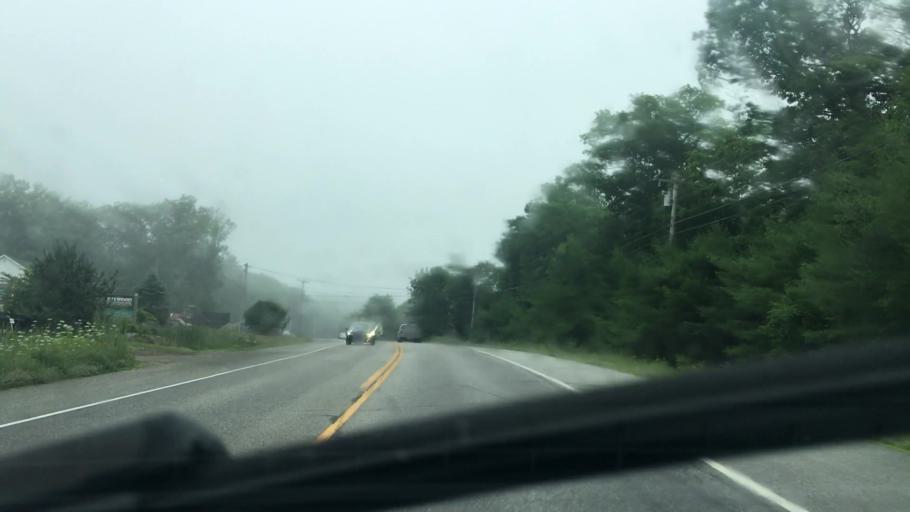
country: US
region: Maine
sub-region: Lincoln County
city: Edgecomb
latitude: 43.9388
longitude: -69.6248
